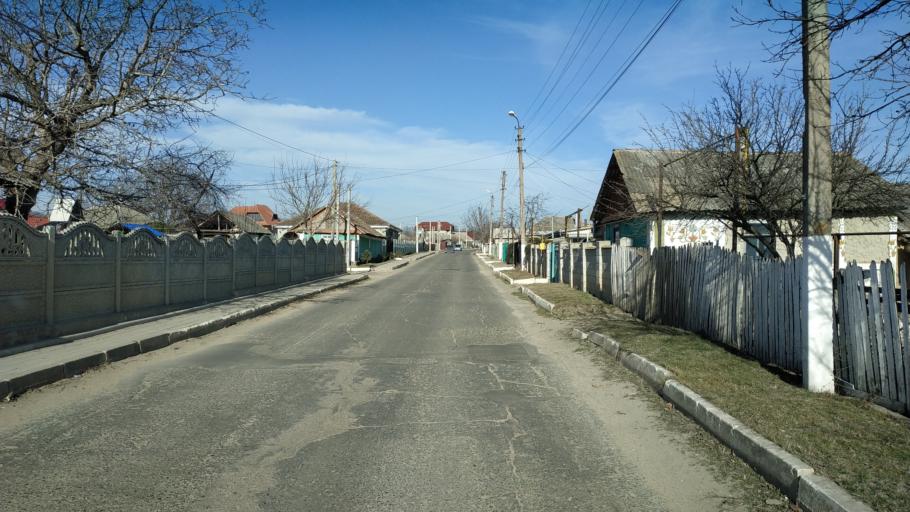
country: MD
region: Chisinau
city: Vatra
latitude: 47.0113
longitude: 28.6623
